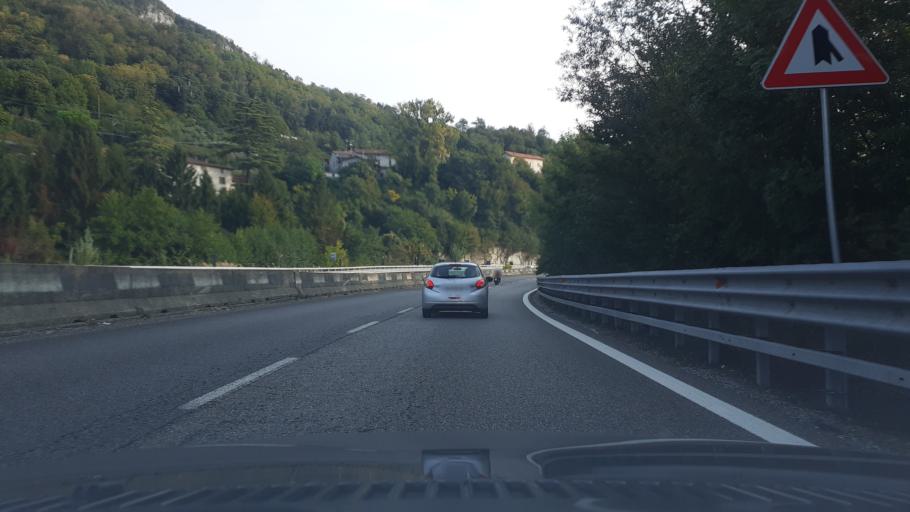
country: IT
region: Lombardy
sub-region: Provincia di Lecco
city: Suello
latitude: 45.8227
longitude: 9.3248
